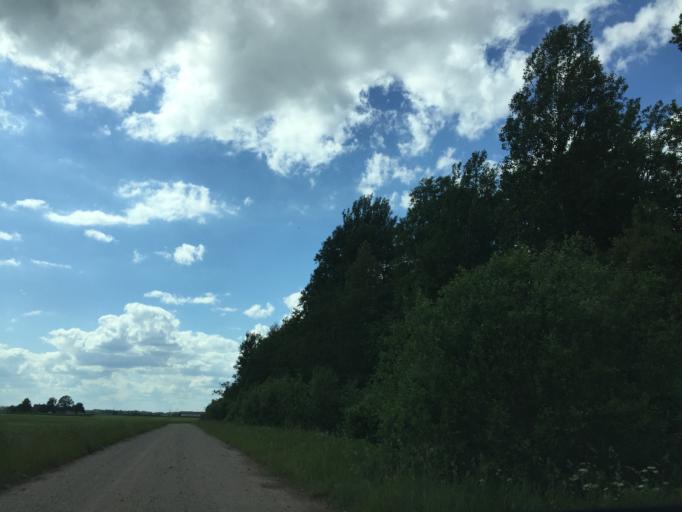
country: LV
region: Engure
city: Smarde
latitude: 56.8679
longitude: 23.3735
